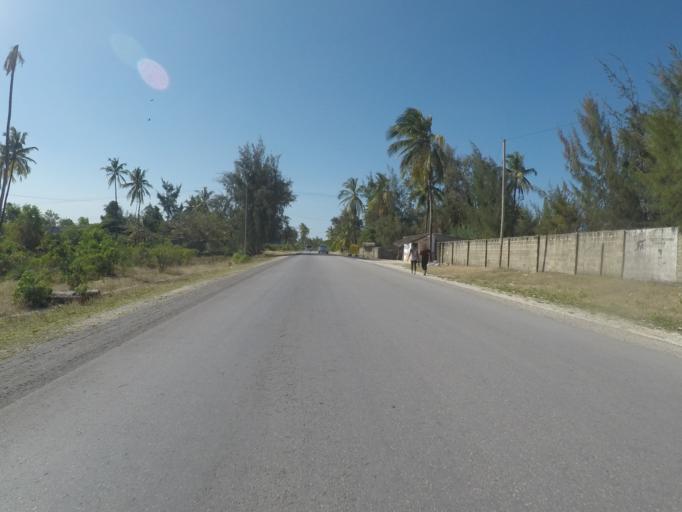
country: TZ
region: Zanzibar Central/South
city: Nganane
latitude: -6.2563
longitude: 39.5325
